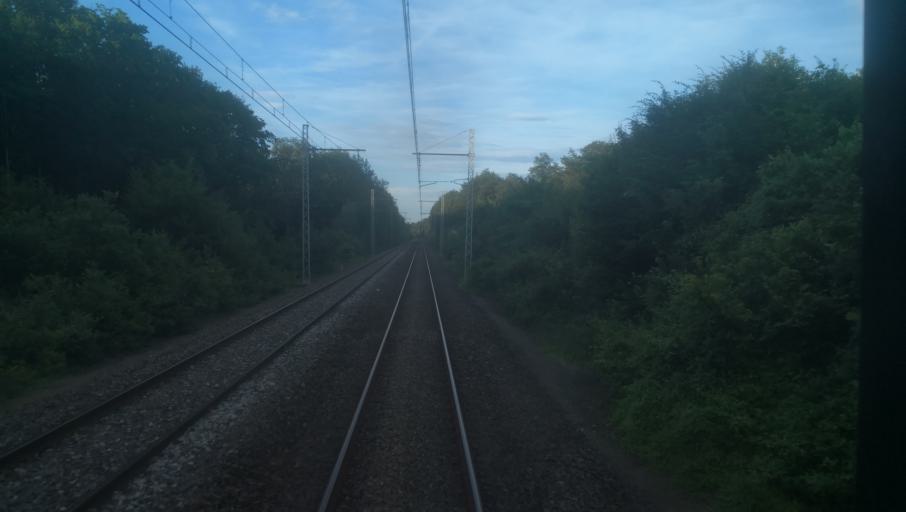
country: FR
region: Centre
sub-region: Departement de l'Indre
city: Saint-Marcel
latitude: 46.6626
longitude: 1.5324
